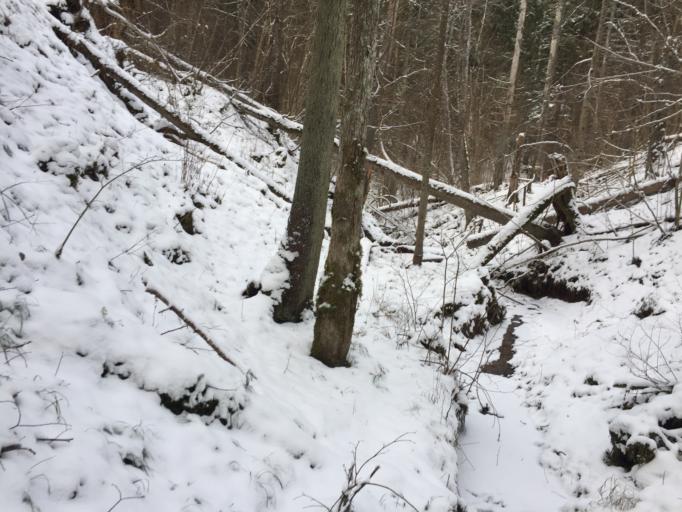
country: LV
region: Amatas Novads
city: Drabesi
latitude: 57.2198
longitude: 25.1679
